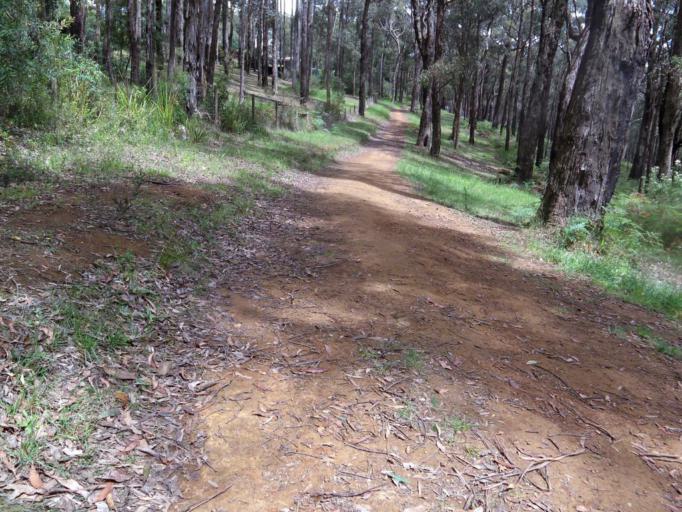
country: AU
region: Victoria
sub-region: Cardinia
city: Cockatoo
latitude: -37.9395
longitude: 145.4750
